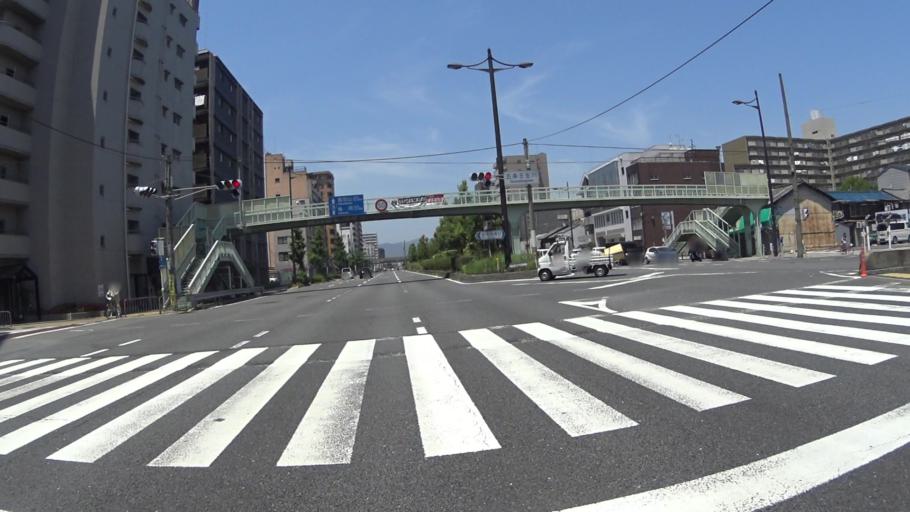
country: JP
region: Kyoto
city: Kyoto
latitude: 34.9962
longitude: 135.7464
